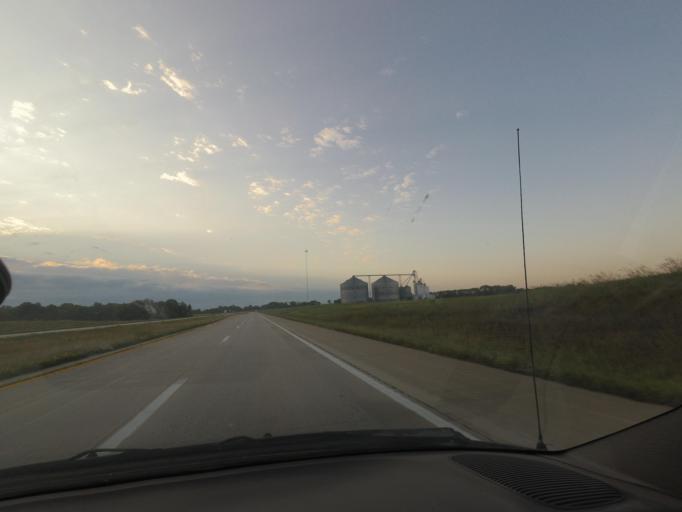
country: US
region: Missouri
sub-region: Shelby County
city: Shelbina
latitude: 39.7462
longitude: -92.2459
